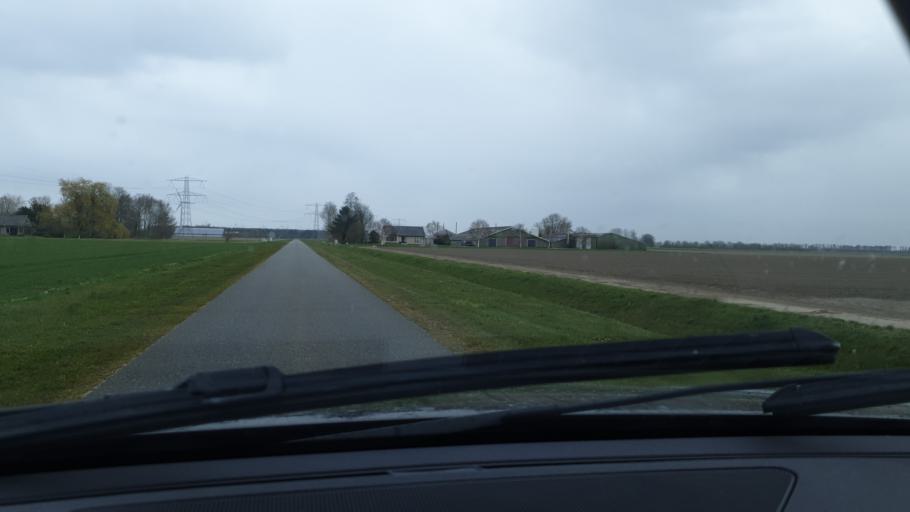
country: NL
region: Flevoland
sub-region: Gemeente Urk
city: Urk
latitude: 52.5754
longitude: 5.5541
